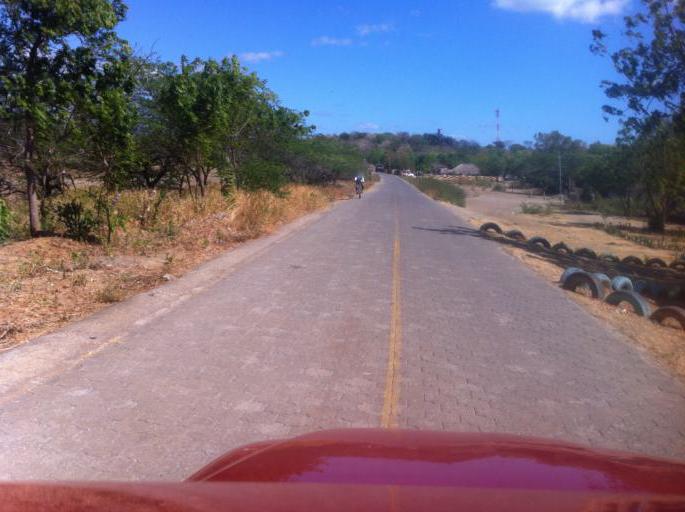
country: NI
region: Carazo
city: El Rosario
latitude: 11.6198
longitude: -86.3270
